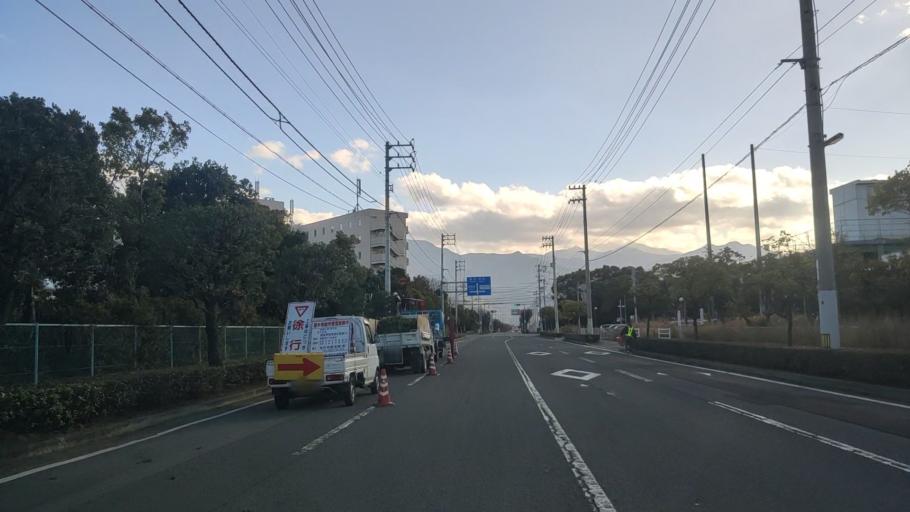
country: JP
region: Ehime
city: Saijo
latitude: 33.9366
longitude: 133.1922
